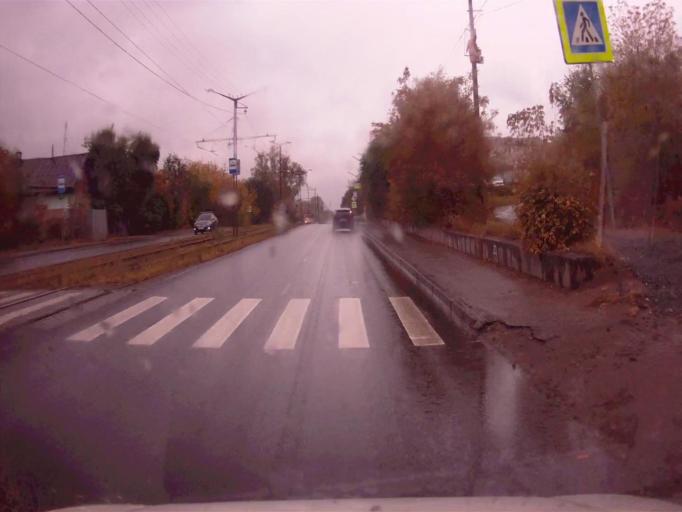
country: RU
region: Chelyabinsk
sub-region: Gorod Chelyabinsk
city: Chelyabinsk
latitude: 55.1738
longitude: 61.4153
